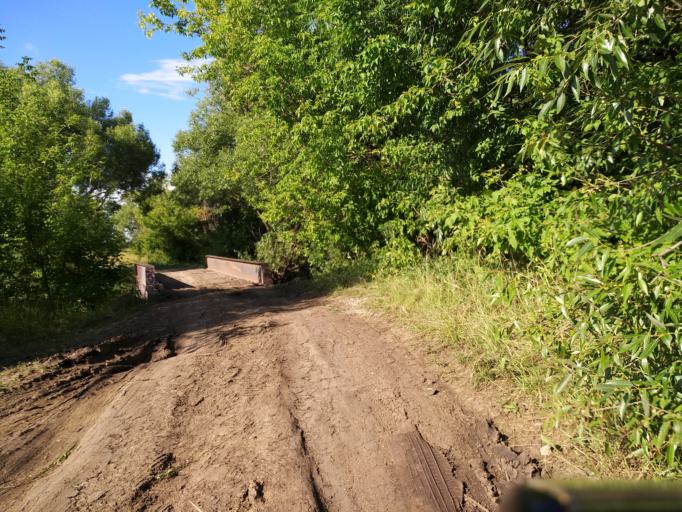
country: RU
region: Lipetsk
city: Dobrinka
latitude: 52.0249
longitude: 40.5603
